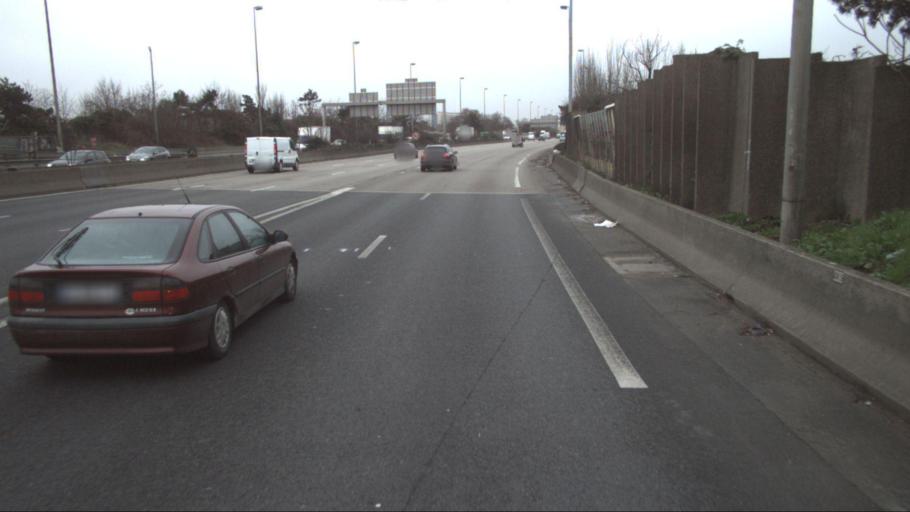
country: FR
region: Ile-de-France
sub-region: Departement du Val-de-Marne
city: Maisons-Alfort
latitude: 48.8123
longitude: 2.4487
